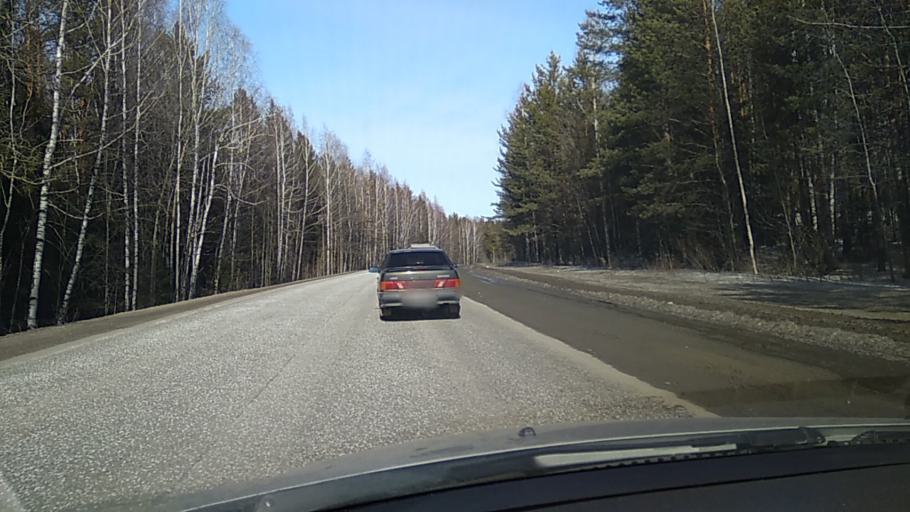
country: RU
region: Sverdlovsk
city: Chernoistochinsk
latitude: 57.7761
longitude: 59.8903
